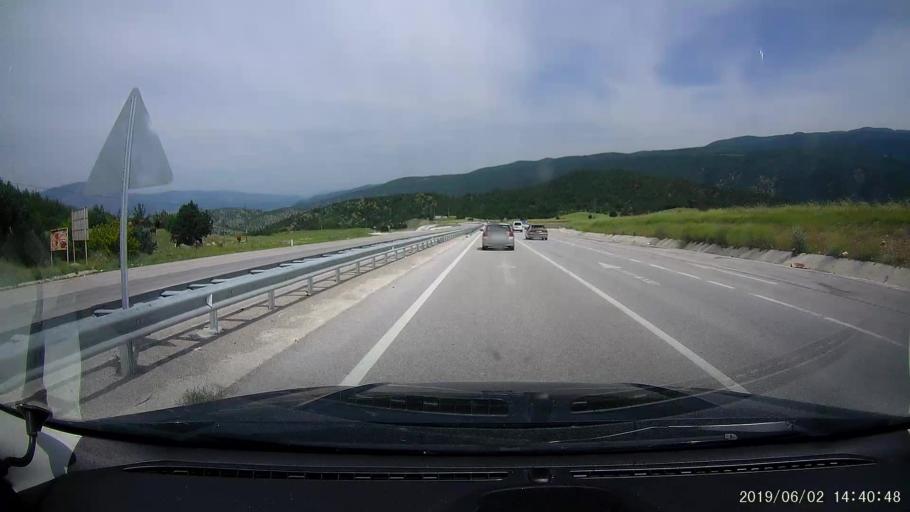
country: TR
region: Corum
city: Hacihamza
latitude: 41.0832
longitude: 34.3269
